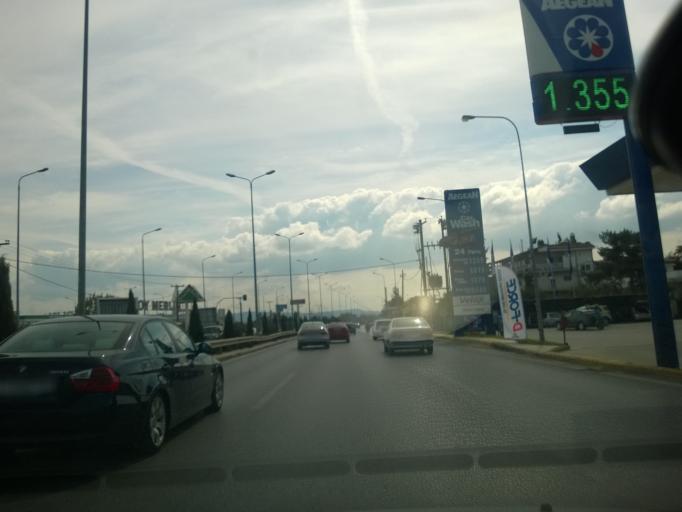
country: GR
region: Central Macedonia
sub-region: Nomos Thessalonikis
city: Thermi
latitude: 40.5542
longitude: 22.9803
